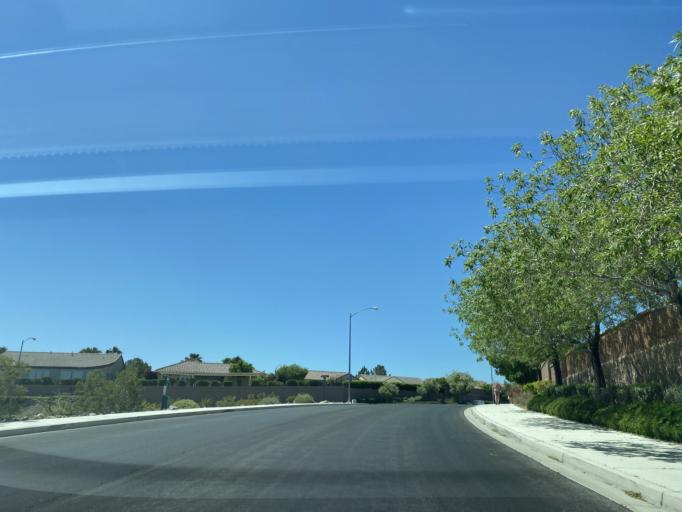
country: US
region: Nevada
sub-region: Clark County
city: Whitney
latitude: 35.9449
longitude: -115.0842
